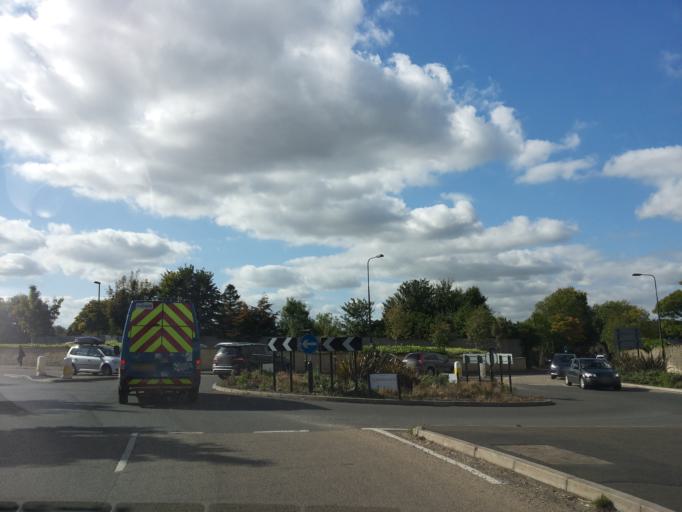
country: GB
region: England
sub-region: Bath and North East Somerset
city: Bath
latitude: 51.3572
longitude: -2.3722
